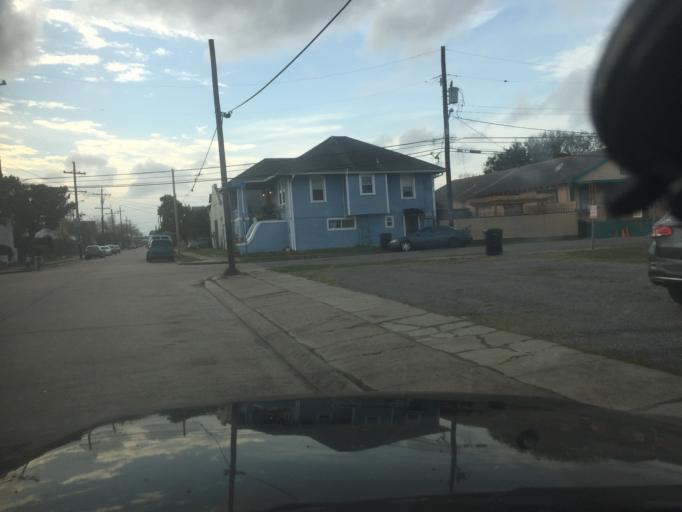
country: US
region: Louisiana
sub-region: Orleans Parish
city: New Orleans
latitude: 29.9859
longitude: -90.0767
